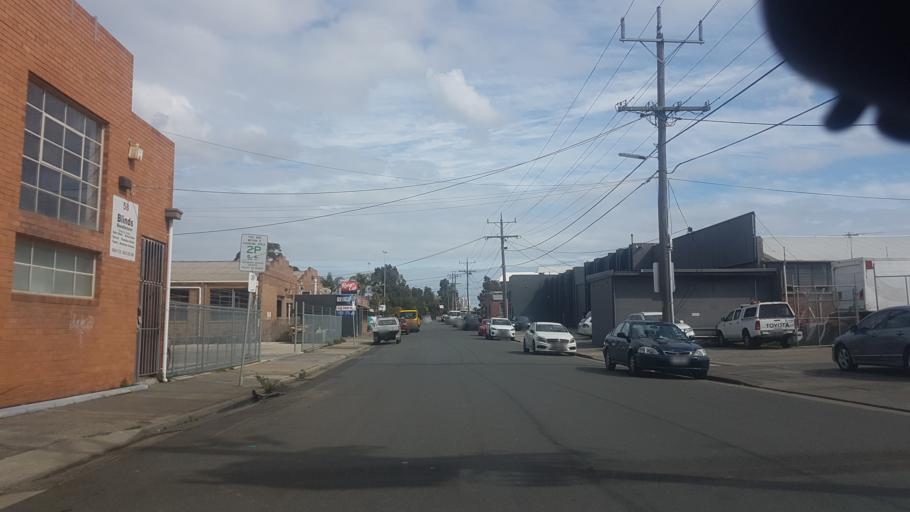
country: AU
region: Victoria
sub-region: Monash
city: Clayton
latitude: -37.9217
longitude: 145.1426
